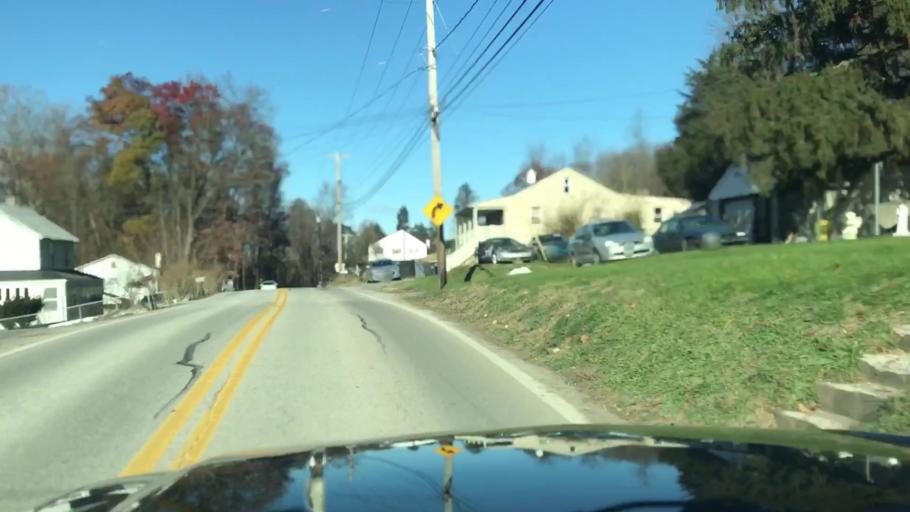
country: US
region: Pennsylvania
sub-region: Cumberland County
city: Lower Allen
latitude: 40.1868
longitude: -76.8873
